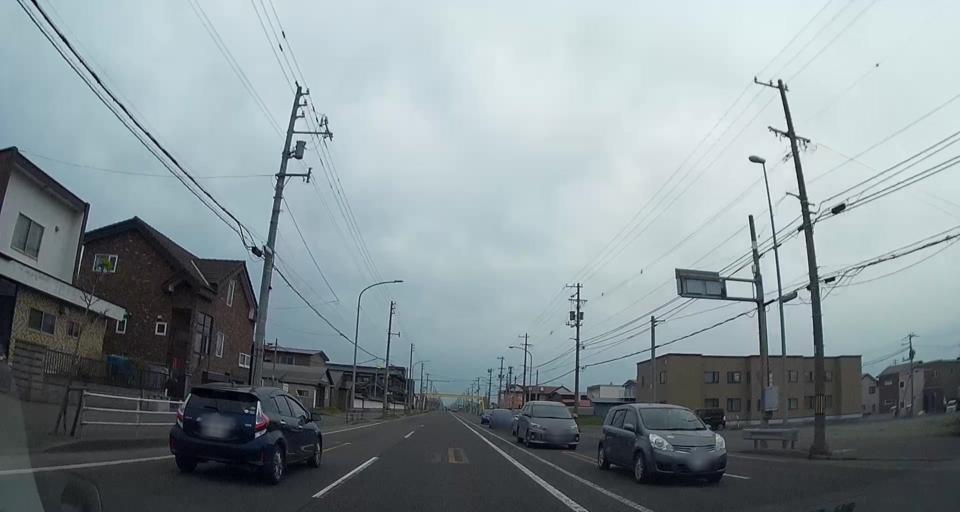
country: JP
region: Hokkaido
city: Tomakomai
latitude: 42.6262
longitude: 141.5908
